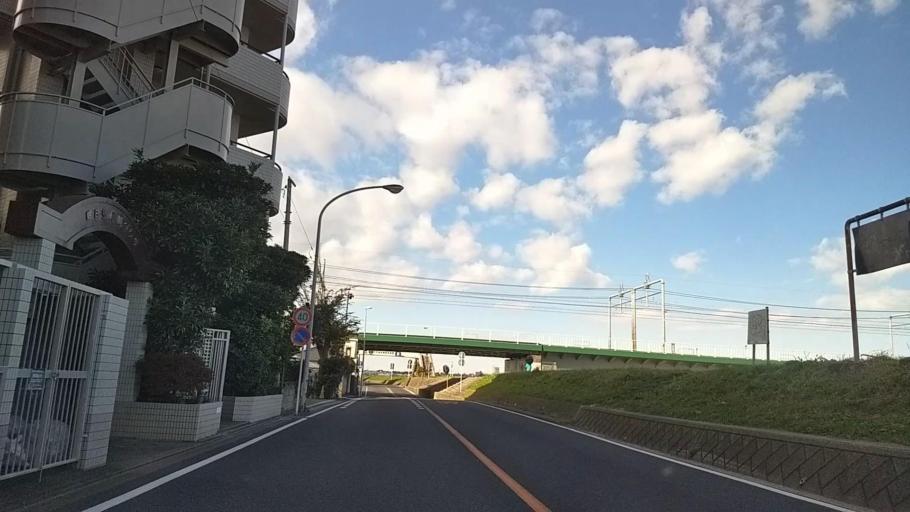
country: JP
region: Kanagawa
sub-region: Kawasaki-shi
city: Kawasaki
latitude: 35.5844
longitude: 139.6653
